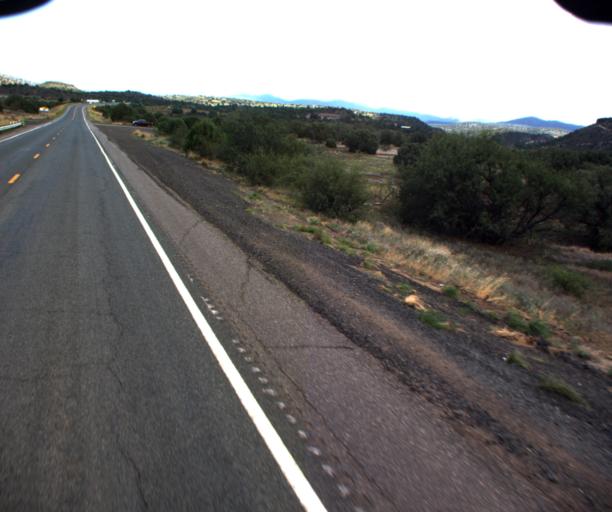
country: US
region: Arizona
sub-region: Yavapai County
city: Camp Verde
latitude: 34.5147
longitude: -112.0008
